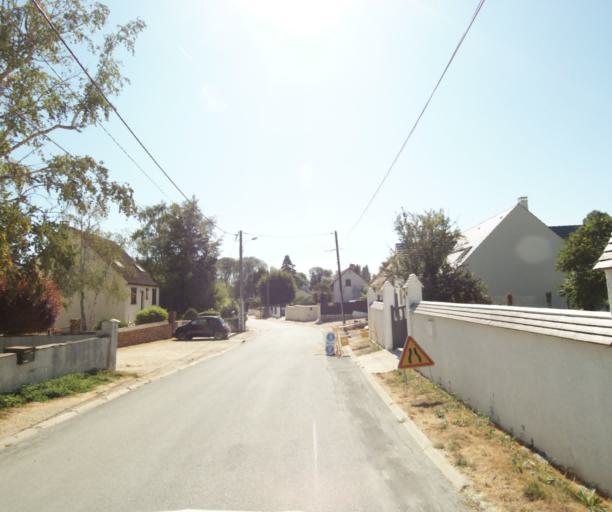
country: FR
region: Ile-de-France
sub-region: Departement de l'Essonne
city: Baulne
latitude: 48.5090
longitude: 2.3603
